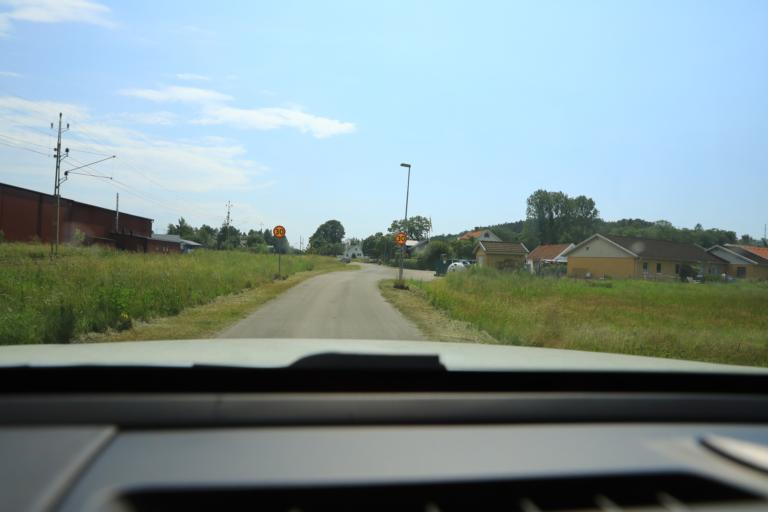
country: SE
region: Halland
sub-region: Varbergs Kommun
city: Varberg
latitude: 57.1750
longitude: 12.3013
